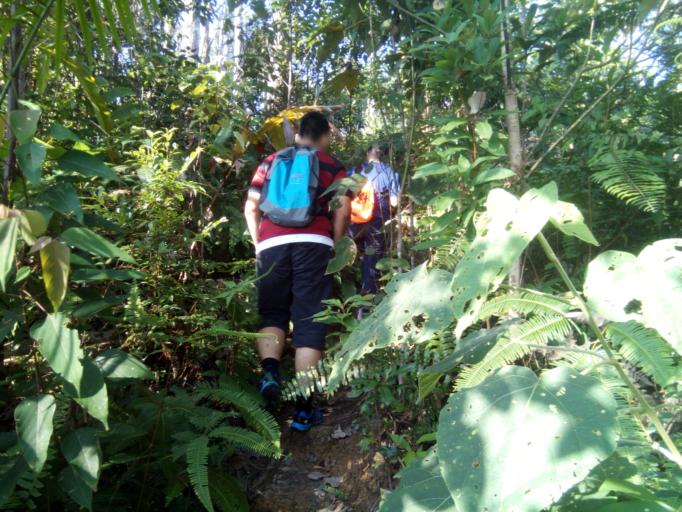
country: MY
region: Penang
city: Tanjung Tokong
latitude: 5.4284
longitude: 100.2844
